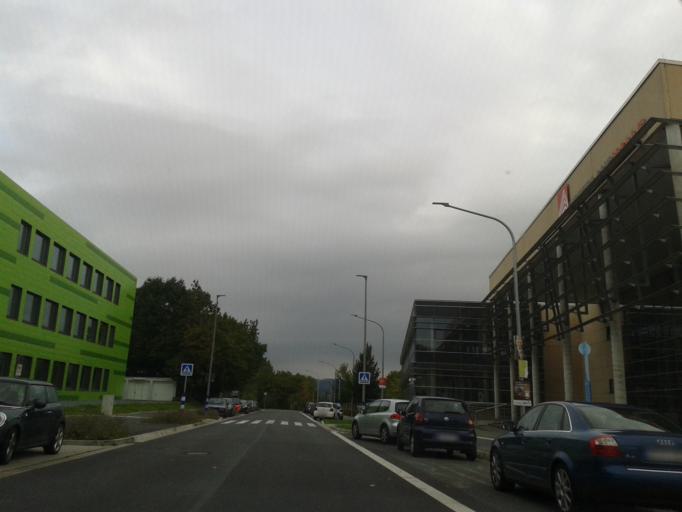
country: DE
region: North Rhine-Westphalia
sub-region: Regierungsbezirk Detmold
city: Lemgo
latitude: 52.0158
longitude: 8.9073
